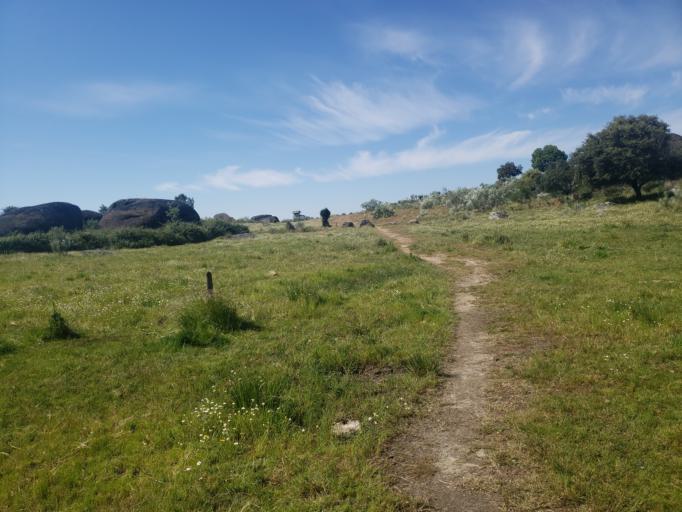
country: ES
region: Extremadura
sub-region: Provincia de Caceres
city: Malpartida de Caceres
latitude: 39.4210
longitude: -6.4993
